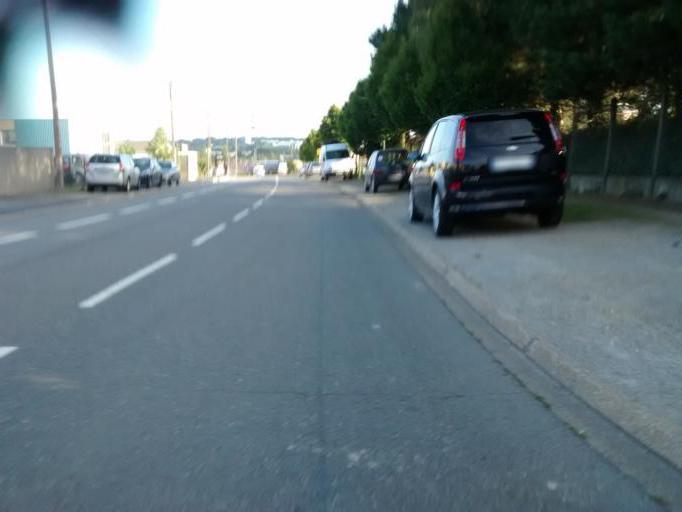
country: FR
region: Brittany
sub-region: Departement d'Ille-et-Vilaine
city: Chantepie
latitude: 48.1053
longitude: -1.6210
